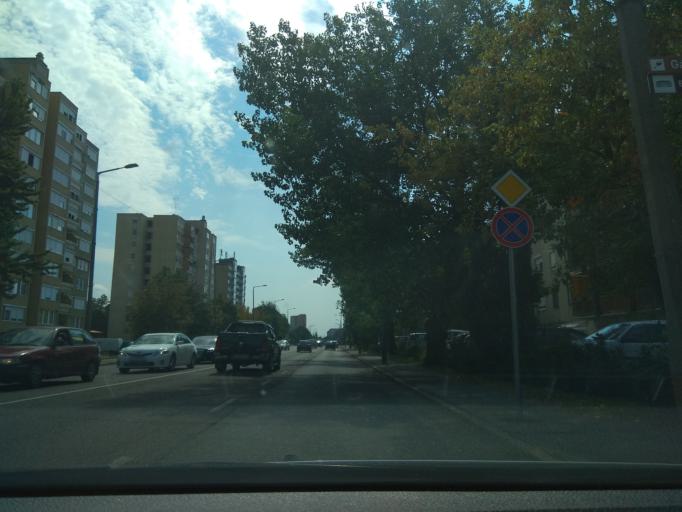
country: HU
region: Heves
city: Eger
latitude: 47.9176
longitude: 20.3696
